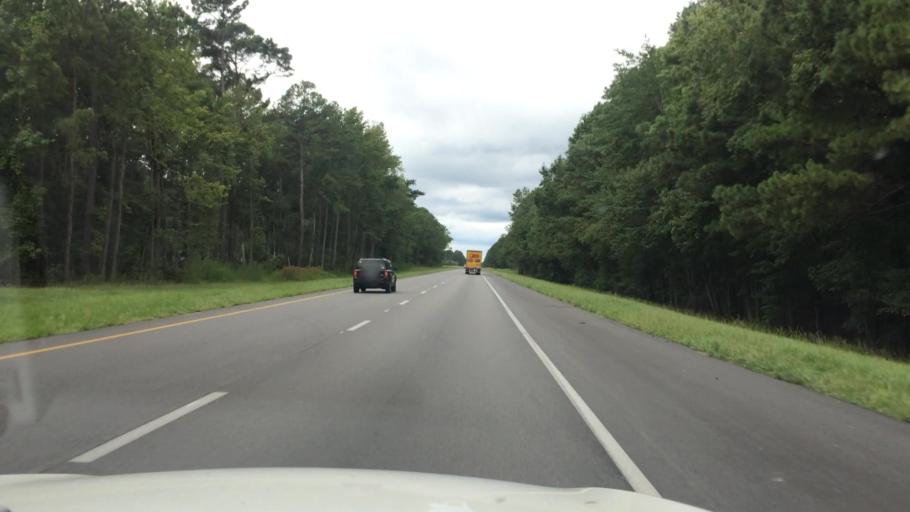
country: US
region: South Carolina
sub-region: Lee County
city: Bishopville
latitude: 34.1961
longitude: -80.2988
